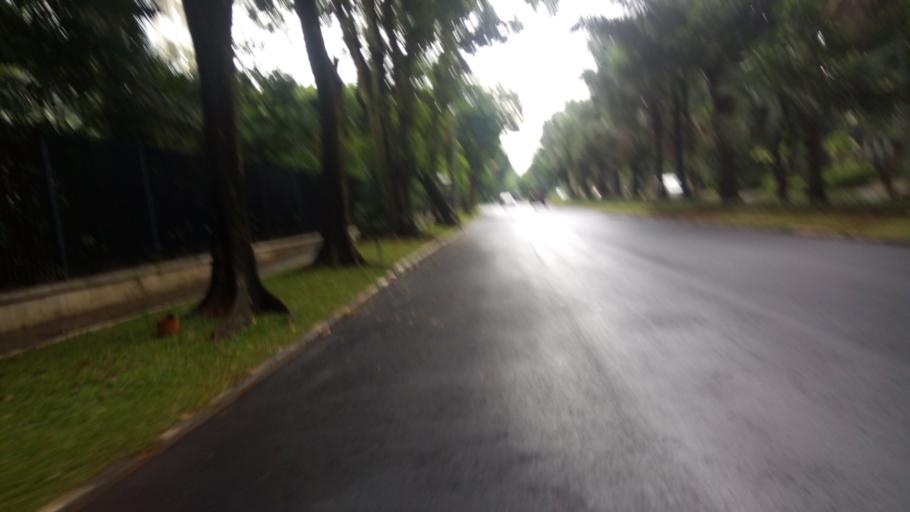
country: ID
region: Jakarta Raya
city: Jakarta
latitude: -6.2532
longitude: 106.8057
